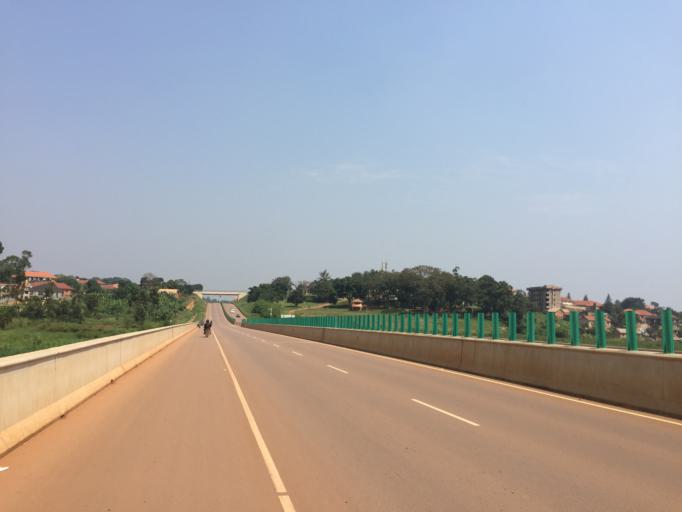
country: UG
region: Central Region
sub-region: Kampala District
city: Kampala
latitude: 0.2374
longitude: 32.6132
